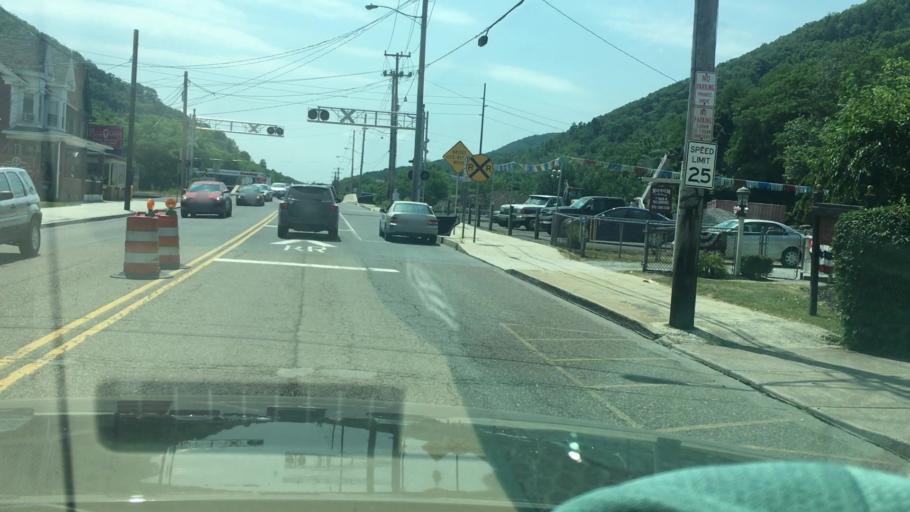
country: US
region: Pennsylvania
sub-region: Schuylkill County
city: Tamaqua
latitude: 40.7946
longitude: -75.9682
